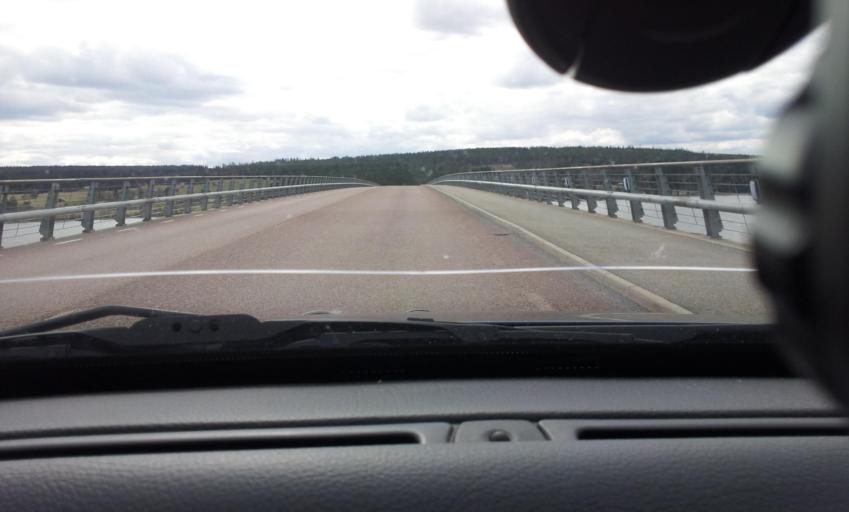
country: SE
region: Jaemtland
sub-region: OEstersunds Kommun
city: Ostersund
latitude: 63.1604
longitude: 14.6014
